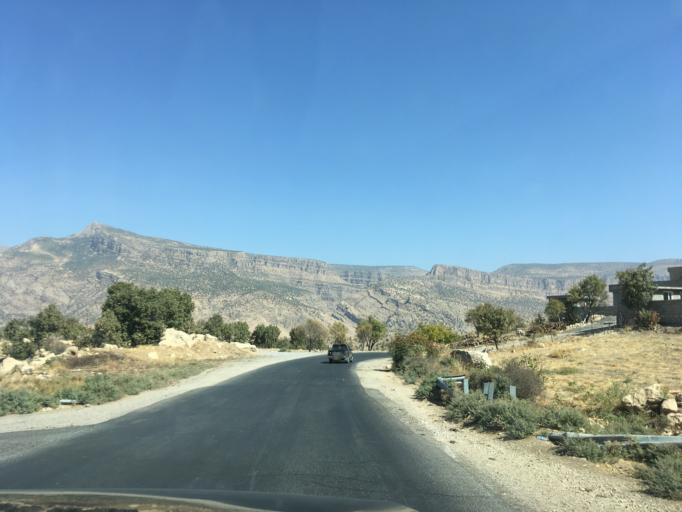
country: IQ
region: Arbil
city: Ruwandiz
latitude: 36.6535
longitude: 44.3541
